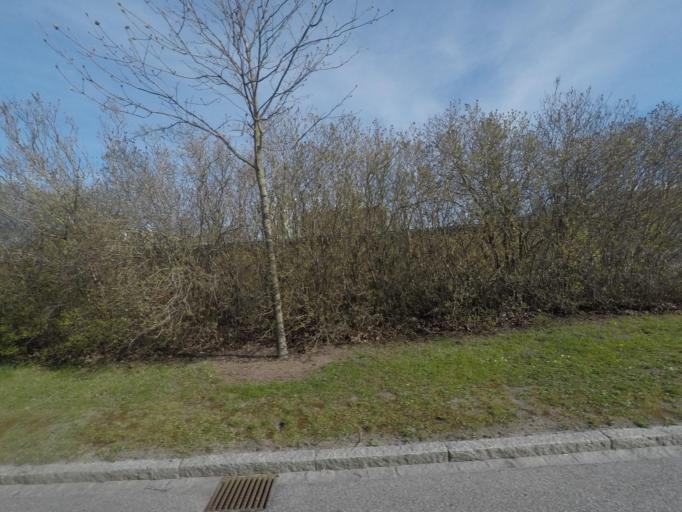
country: SE
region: Skane
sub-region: Malmo
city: Tygelsjo
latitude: 55.5568
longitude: 13.0071
